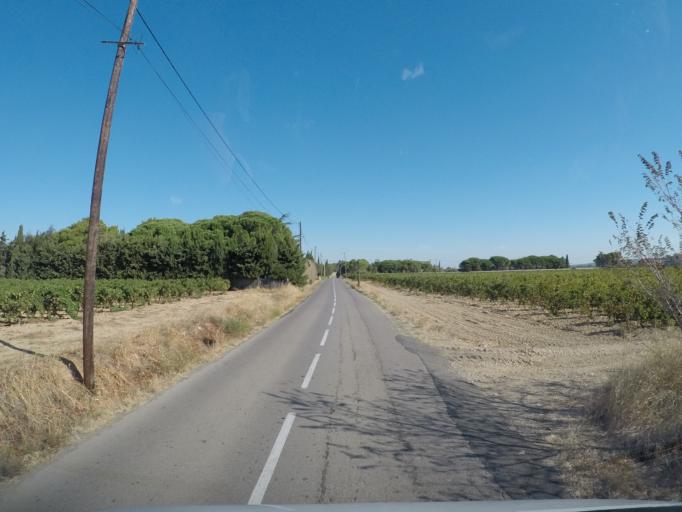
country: FR
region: Languedoc-Roussillon
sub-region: Departement de l'Aude
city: Narbonne
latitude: 43.1516
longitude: 3.0084
